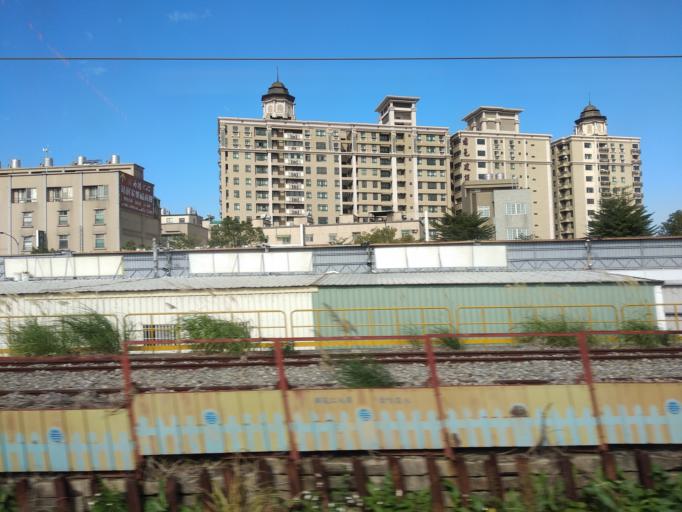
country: TW
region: Taiwan
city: Taoyuan City
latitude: 24.9782
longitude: 121.2719
